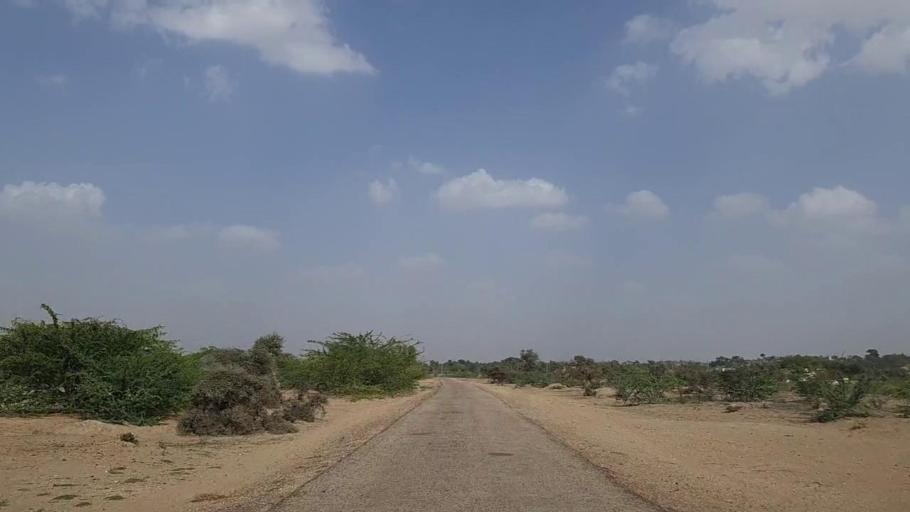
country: PK
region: Sindh
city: Islamkot
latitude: 24.8296
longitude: 70.1778
